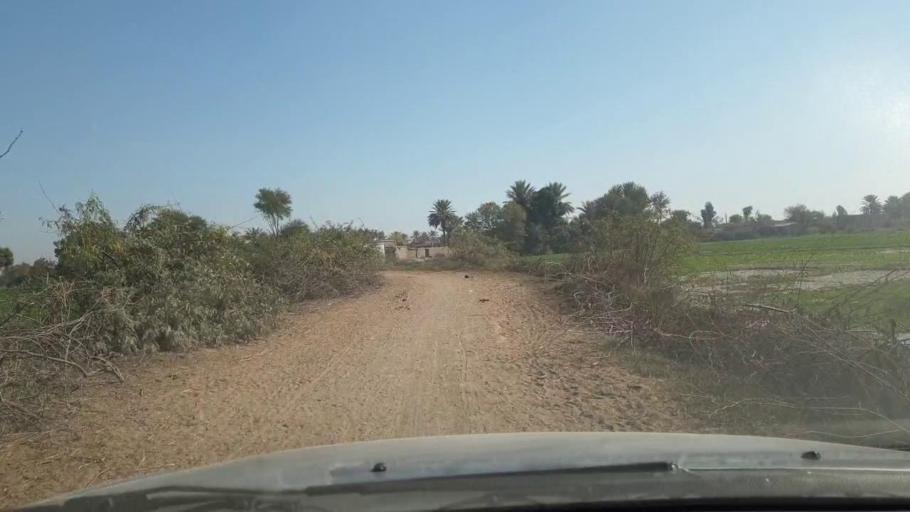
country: PK
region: Sindh
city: Adilpur
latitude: 27.8945
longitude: 69.2568
